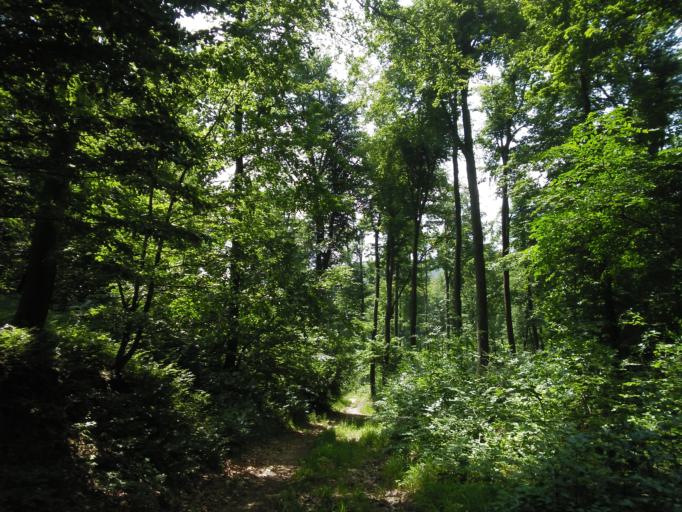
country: HU
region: Pest
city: Pilisszentkereszt
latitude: 47.7118
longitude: 18.8712
